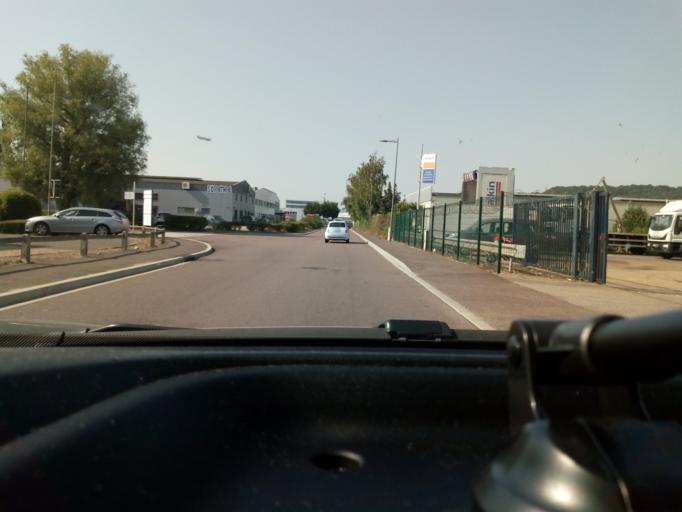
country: FR
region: Haute-Normandie
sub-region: Departement de la Seine-Maritime
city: Saint-Etienne-du-Rouvray
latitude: 49.4003
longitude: 1.1146
